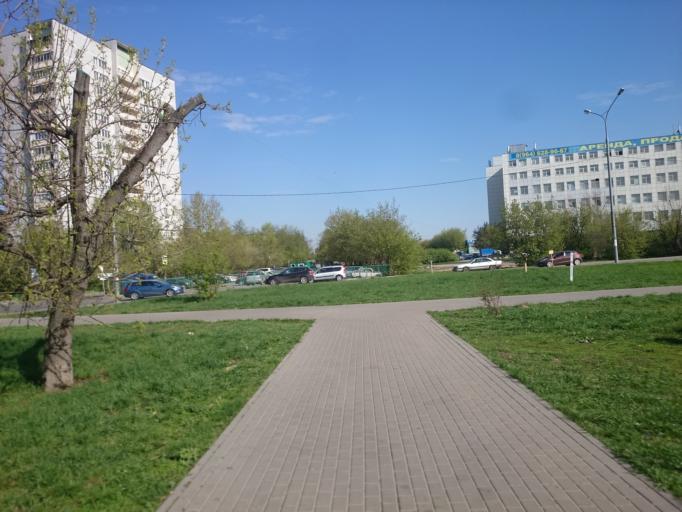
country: RU
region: Moscow
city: Tekstil'shchiki
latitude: 55.7198
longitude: 37.7406
